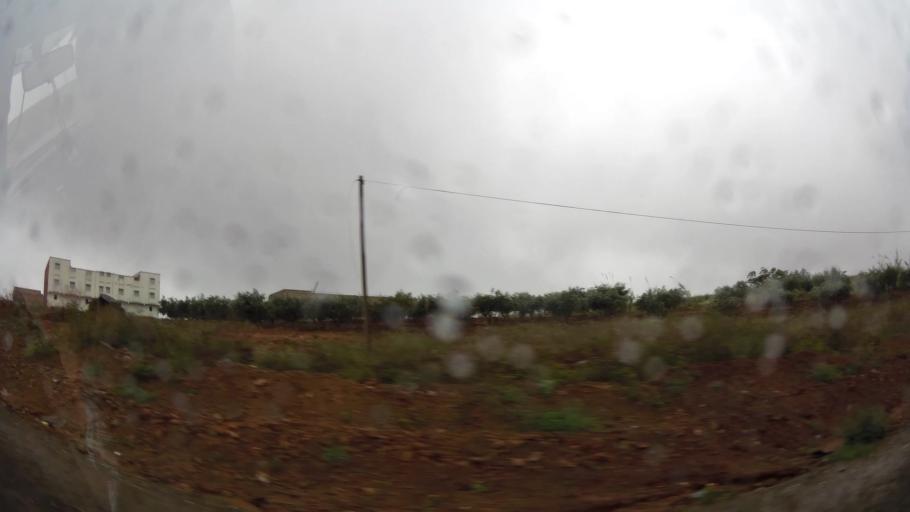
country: MA
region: Oriental
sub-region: Nador
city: Boudinar
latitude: 35.1255
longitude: -3.6288
